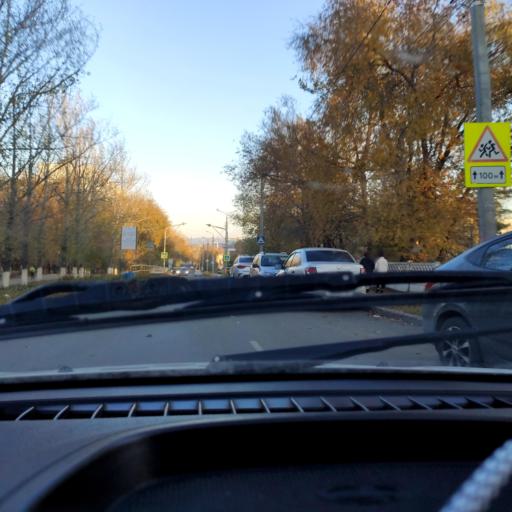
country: RU
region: Samara
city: Zhigulevsk
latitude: 53.4771
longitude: 49.4680
